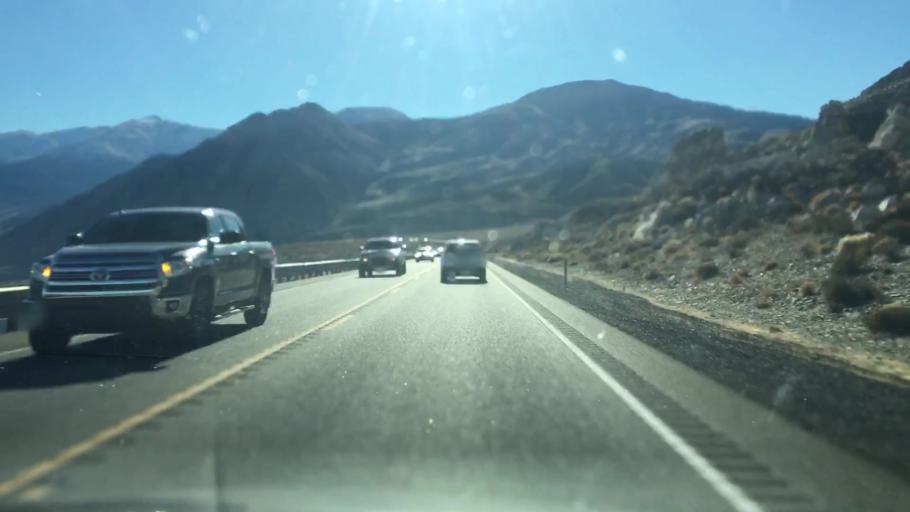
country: US
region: Nevada
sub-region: Mineral County
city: Hawthorne
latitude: 38.7049
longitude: -118.7659
